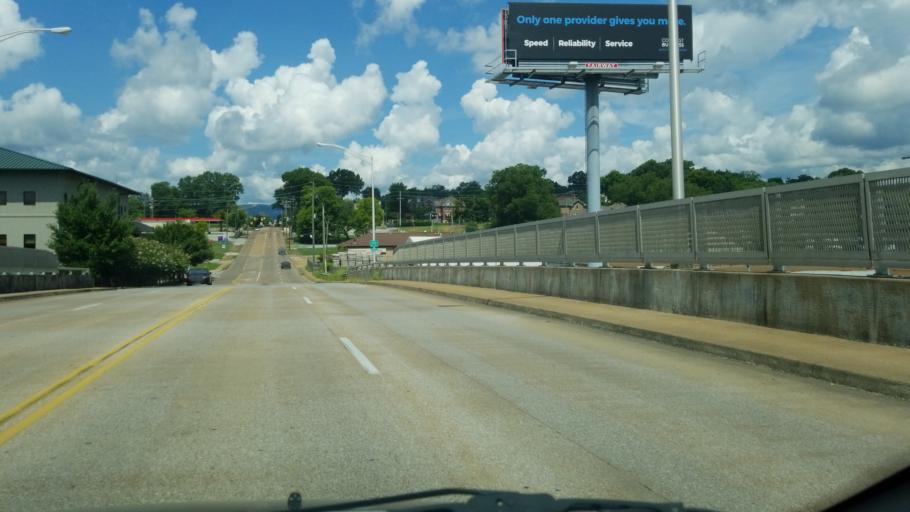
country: US
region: Tennessee
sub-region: Hamilton County
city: Chattanooga
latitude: 35.0408
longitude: -85.2878
